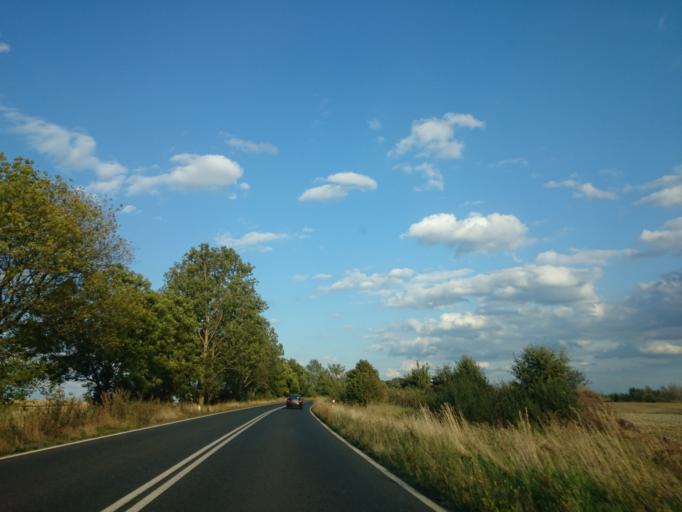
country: PL
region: West Pomeranian Voivodeship
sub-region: Powiat mysliborski
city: Nowogrodek Pomorski
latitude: 52.9035
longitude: 14.9798
